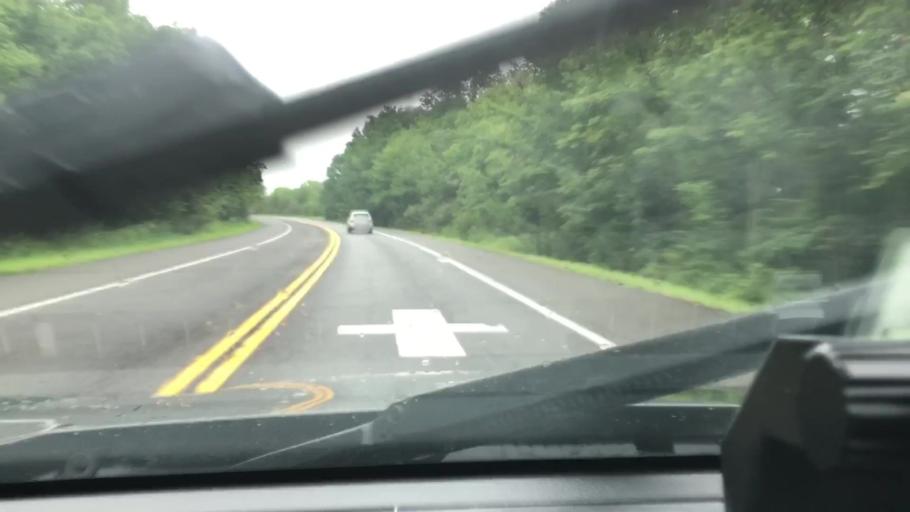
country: US
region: Pennsylvania
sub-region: Bucks County
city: Spinnerstown
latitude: 40.4137
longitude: -75.4612
